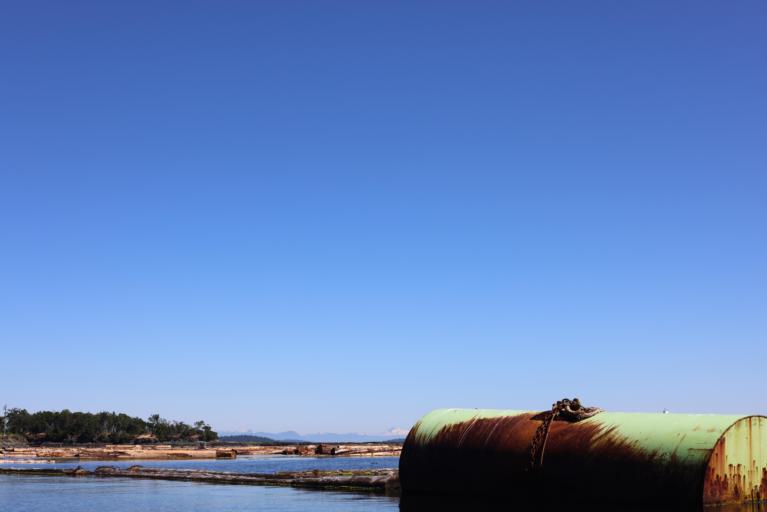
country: CA
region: British Columbia
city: North Cowichan
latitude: 48.8770
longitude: -123.6318
